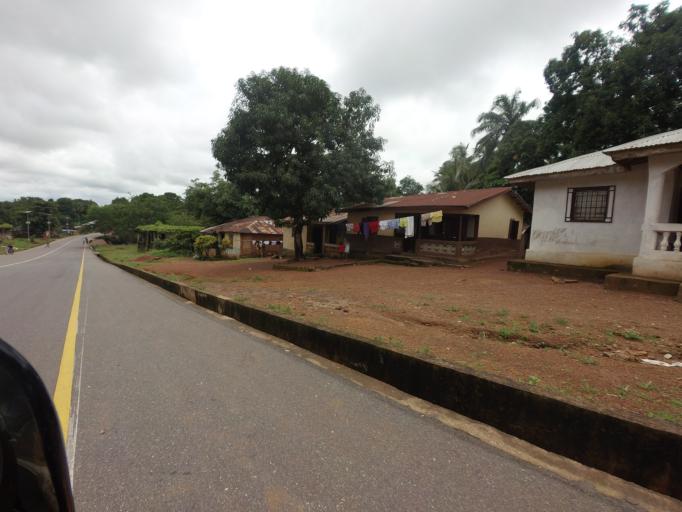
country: SL
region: Northern Province
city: Kambia
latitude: 9.1236
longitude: -12.9193
